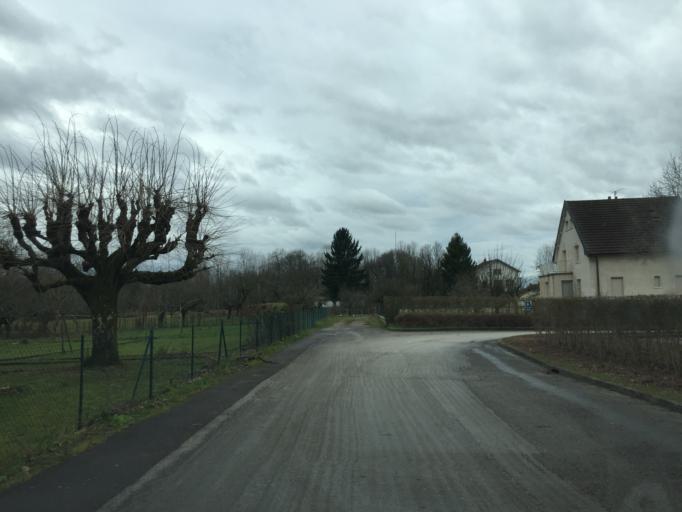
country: FR
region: Franche-Comte
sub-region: Departement du Doubs
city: Arc-et-Senans
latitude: 47.0309
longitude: 5.7791
